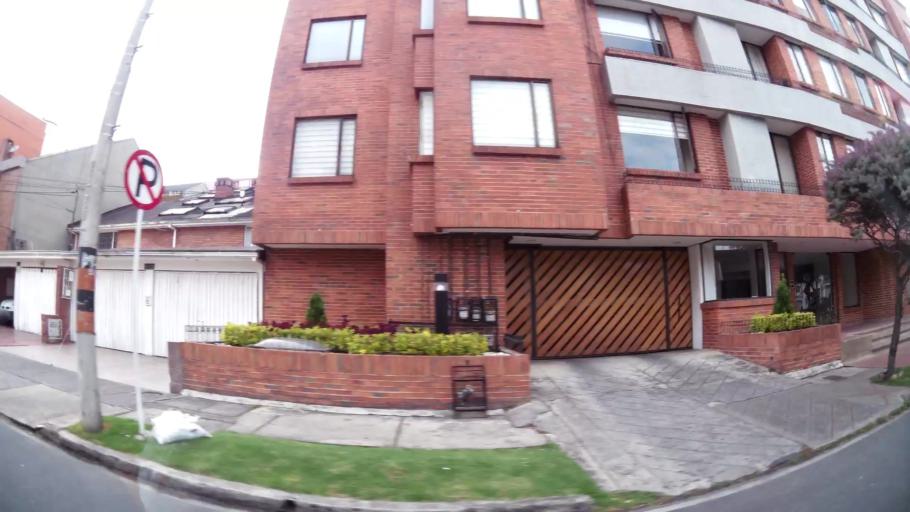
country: CO
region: Bogota D.C.
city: Barrio San Luis
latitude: 4.6990
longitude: -74.0406
